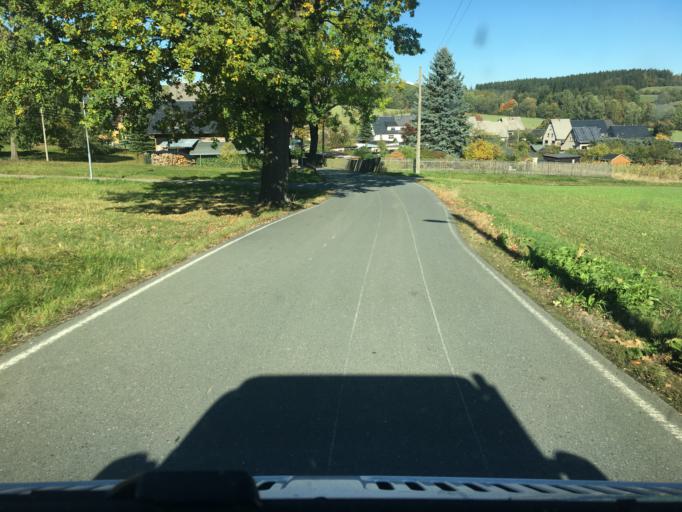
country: DE
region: Saxony
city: Schneeberg
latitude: 50.6029
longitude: 12.6173
